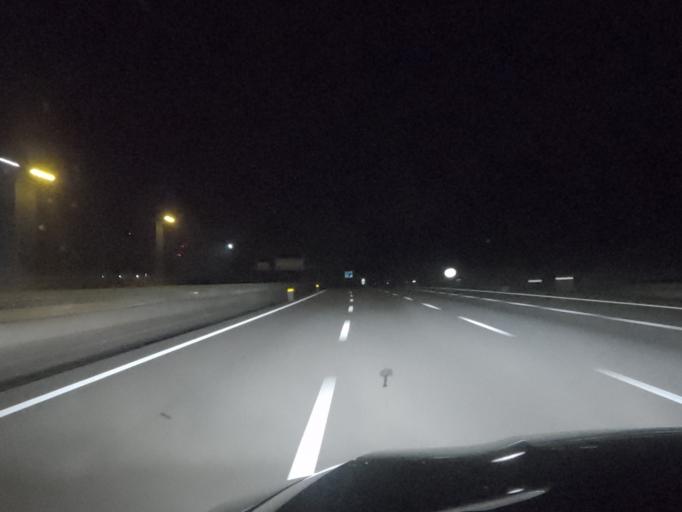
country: PT
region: Aveiro
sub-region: Estarreja
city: Beduido
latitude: 40.7835
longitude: -8.5452
